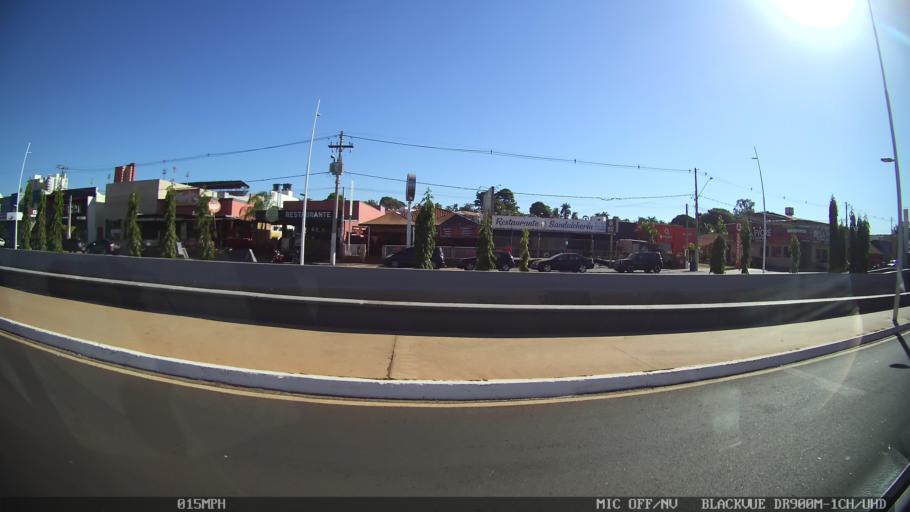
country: BR
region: Sao Paulo
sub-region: Olimpia
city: Olimpia
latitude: -20.7317
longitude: -48.9129
